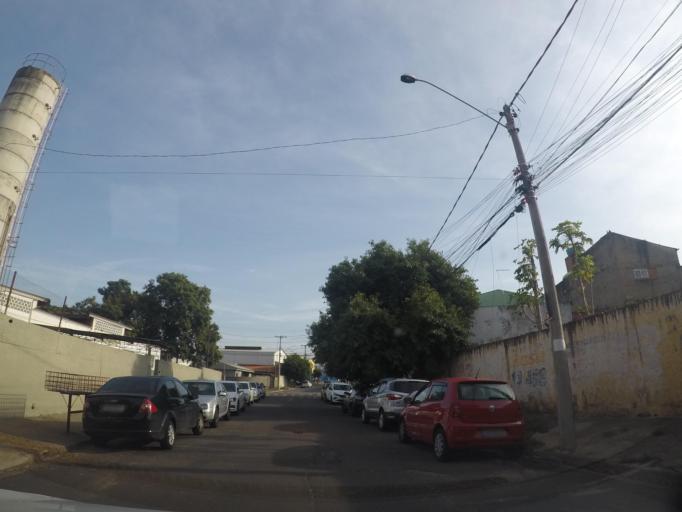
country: BR
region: Sao Paulo
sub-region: Hortolandia
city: Hortolandia
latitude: -22.8267
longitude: -47.1897
